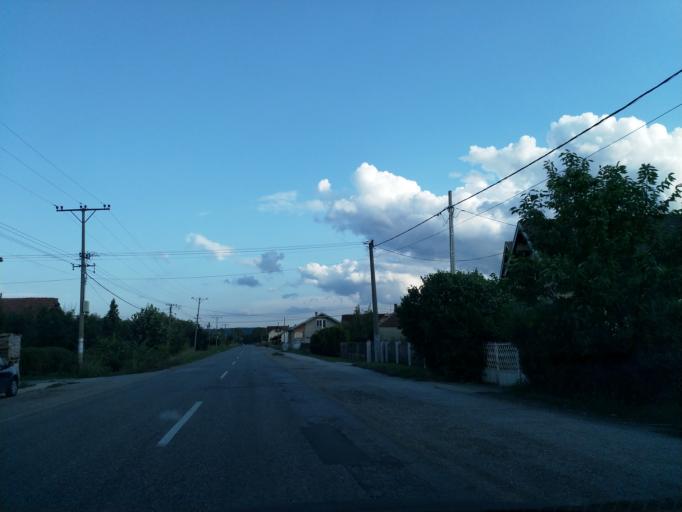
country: RS
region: Central Serbia
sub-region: Rasinski Okrug
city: Cicevac
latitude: 43.7606
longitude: 21.4318
